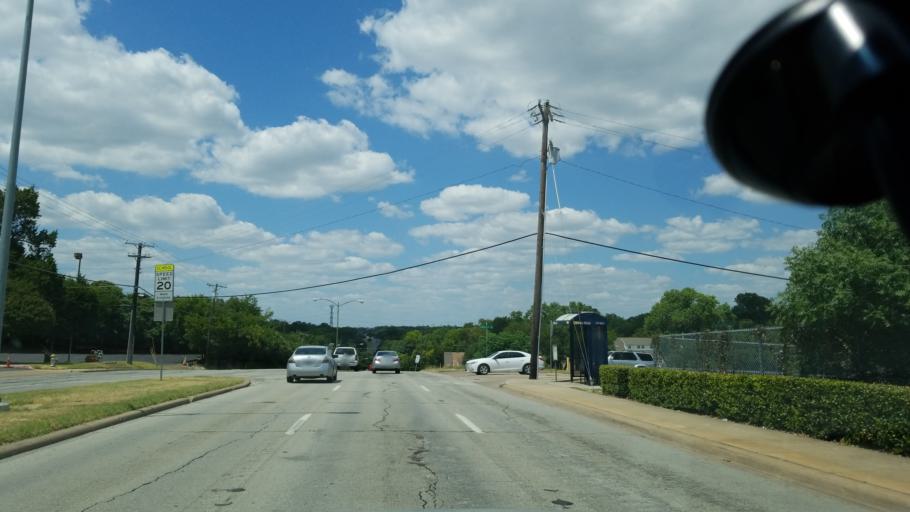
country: US
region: Texas
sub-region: Dallas County
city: Cockrell Hill
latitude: 32.6931
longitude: -96.8570
